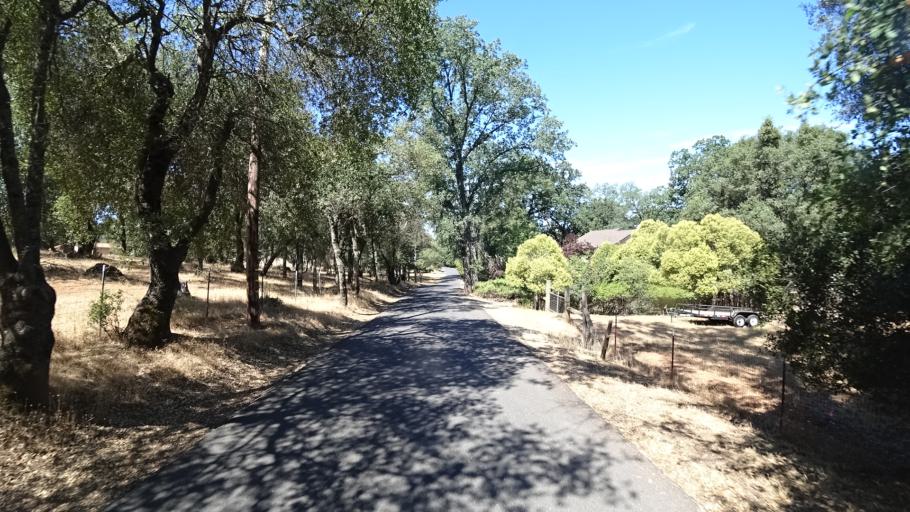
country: US
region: California
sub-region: Calaveras County
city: Angels Camp
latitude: 38.0609
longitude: -120.5378
